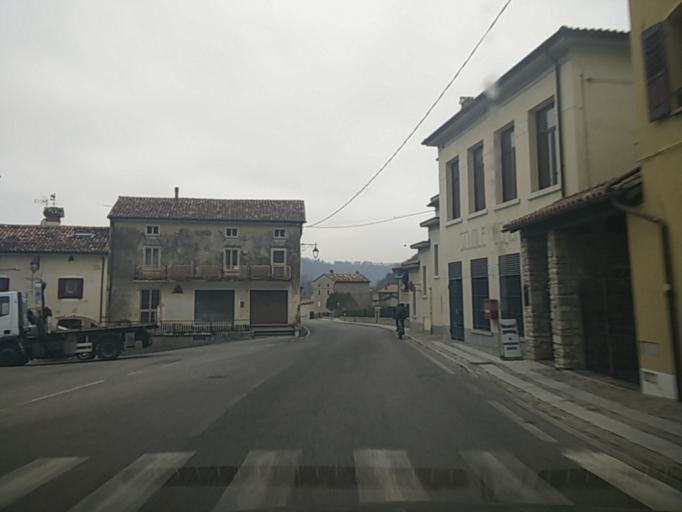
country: IT
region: Veneto
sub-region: Provincia di Treviso
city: Cison di Valmarino
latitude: 45.9786
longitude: 12.1749
